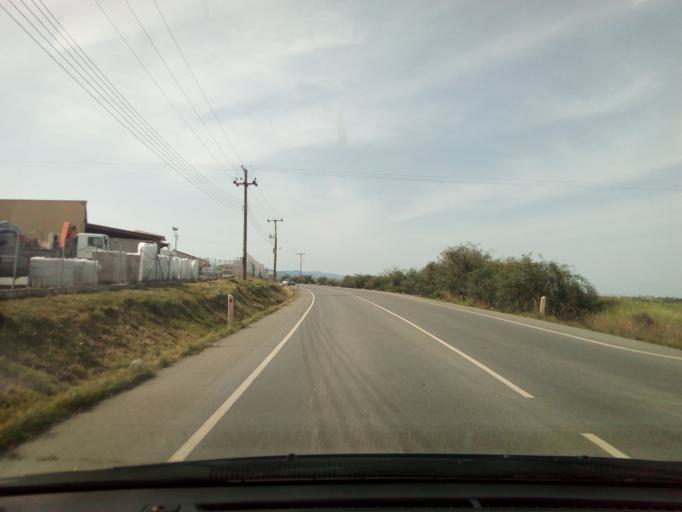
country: CY
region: Lefkosia
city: Arediou
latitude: 35.0515
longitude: 33.1903
